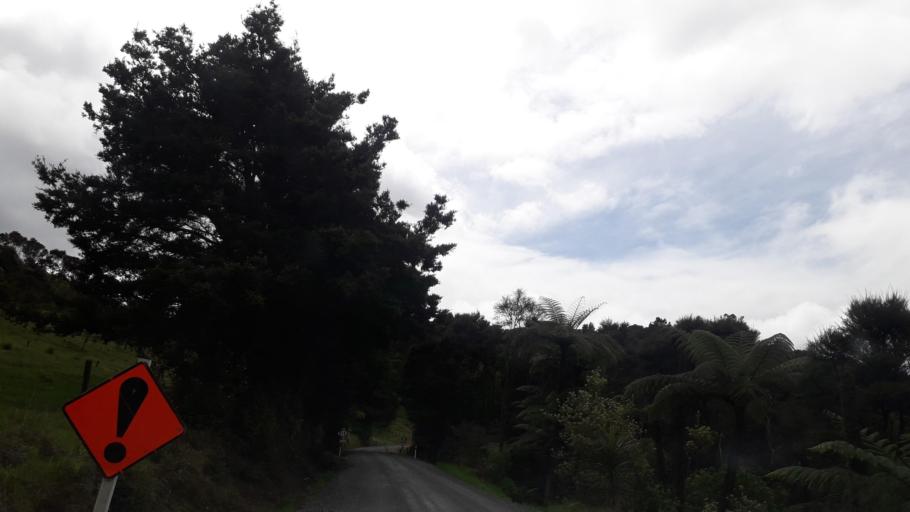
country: NZ
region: Northland
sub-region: Far North District
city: Taipa
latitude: -35.0550
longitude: 173.5559
